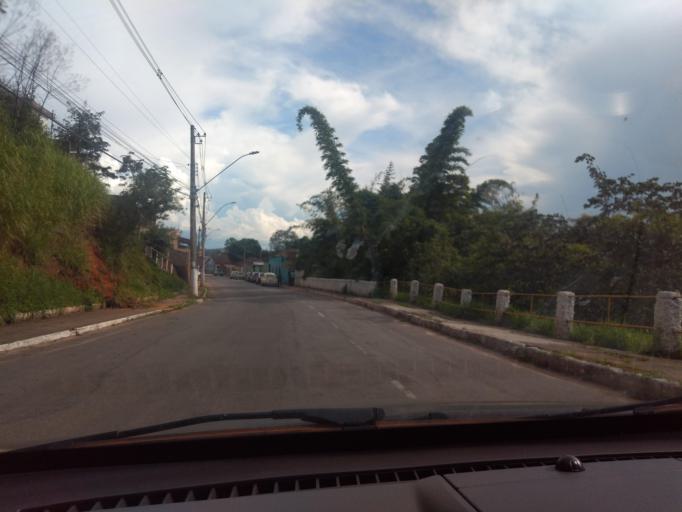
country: BR
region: Minas Gerais
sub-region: Tres Coracoes
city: Tres Coracoes
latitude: -21.7053
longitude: -45.2661
